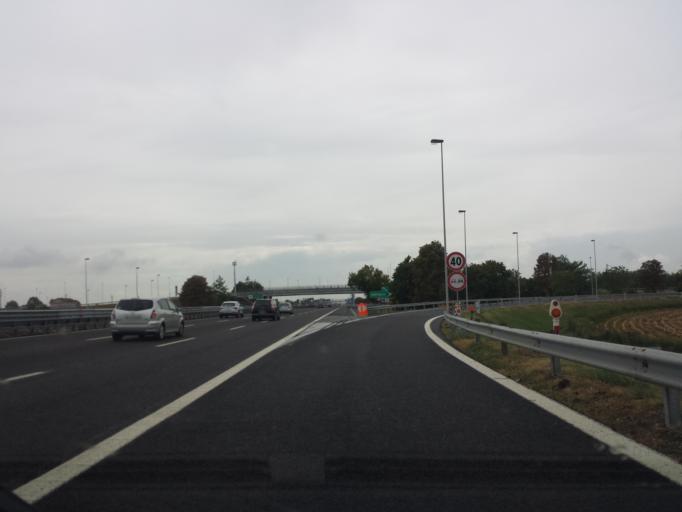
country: IT
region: Veneto
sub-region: Provincia di Vicenza
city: Gambellara
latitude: 45.4374
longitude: 11.3581
